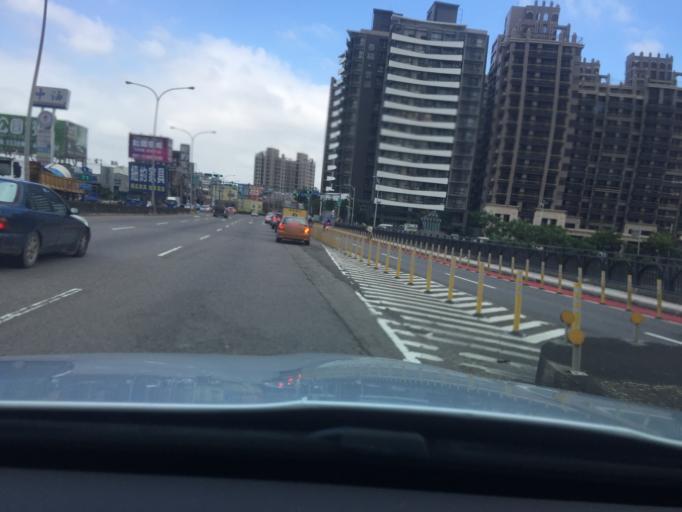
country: TW
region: Taiwan
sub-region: Hsinchu
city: Zhubei
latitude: 24.8245
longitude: 120.9971
